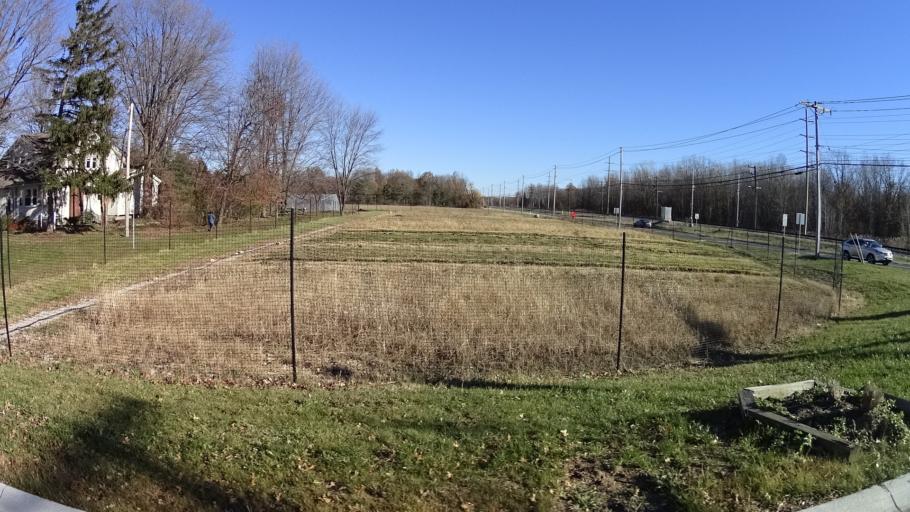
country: US
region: Ohio
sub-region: Lorain County
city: Avon Center
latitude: 41.4785
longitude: -81.9885
